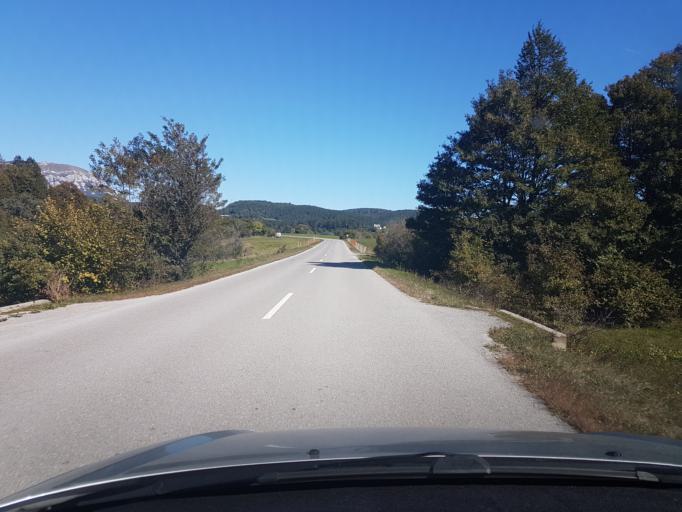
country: SI
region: Divaca
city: Divaca
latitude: 45.7246
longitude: 14.0037
